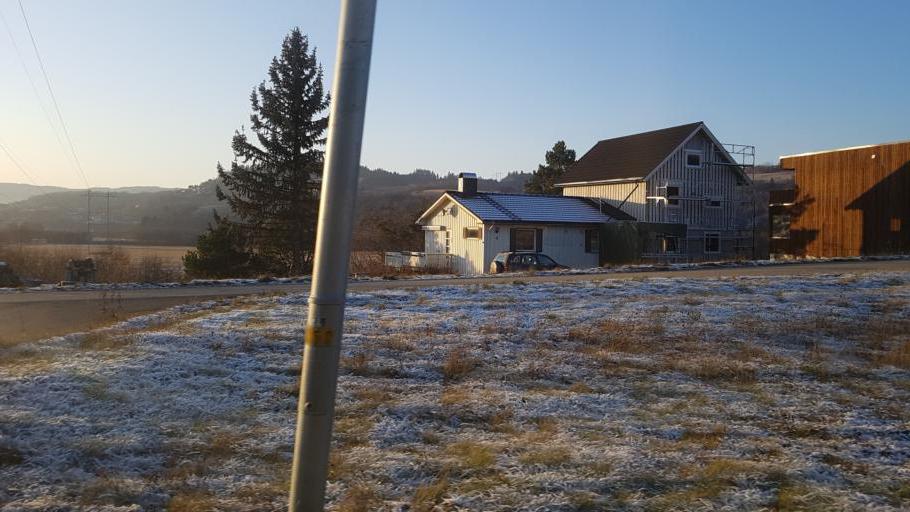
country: NO
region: Sor-Trondelag
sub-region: Melhus
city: Melhus
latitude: 63.2988
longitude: 10.2849
